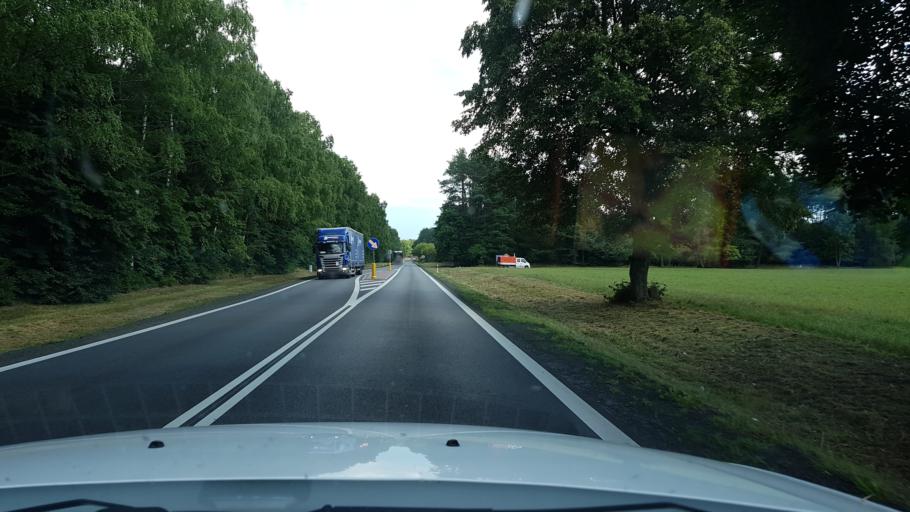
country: PL
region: West Pomeranian Voivodeship
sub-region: Powiat walecki
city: Walcz
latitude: 53.3125
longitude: 16.3626
